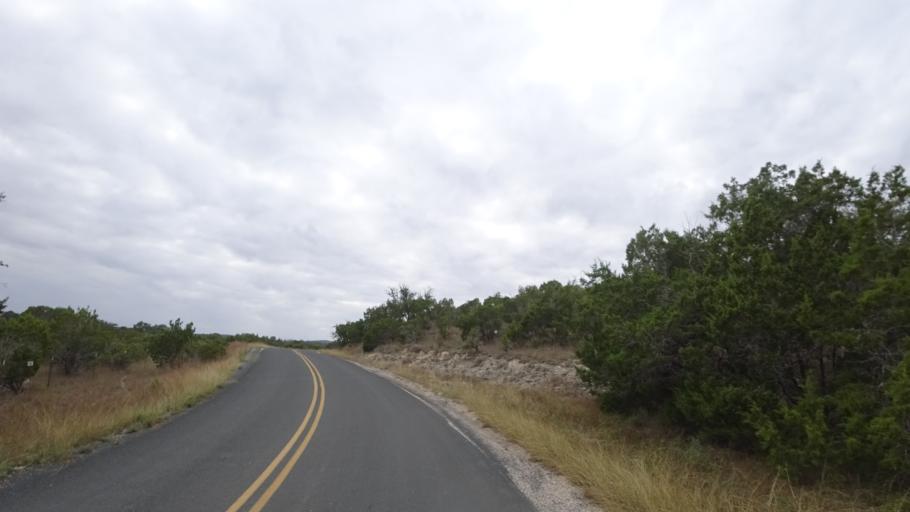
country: US
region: Texas
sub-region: Travis County
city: Bee Cave
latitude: 30.3537
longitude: -97.9272
